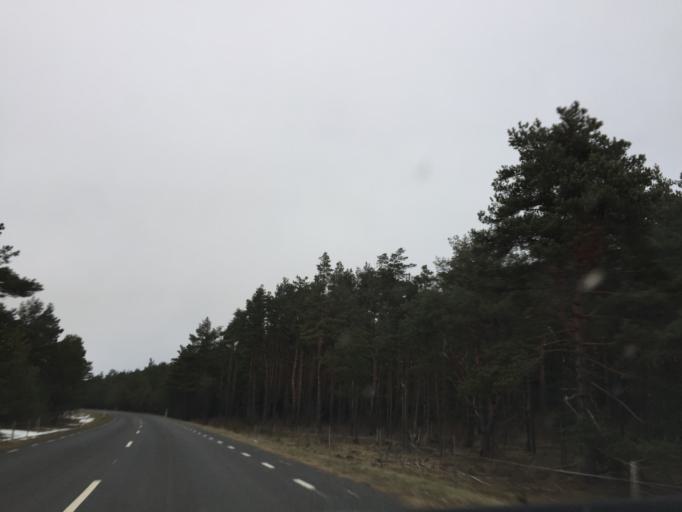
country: EE
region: Saare
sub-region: Kuressaare linn
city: Kuressaare
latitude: 58.5452
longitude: 22.3371
